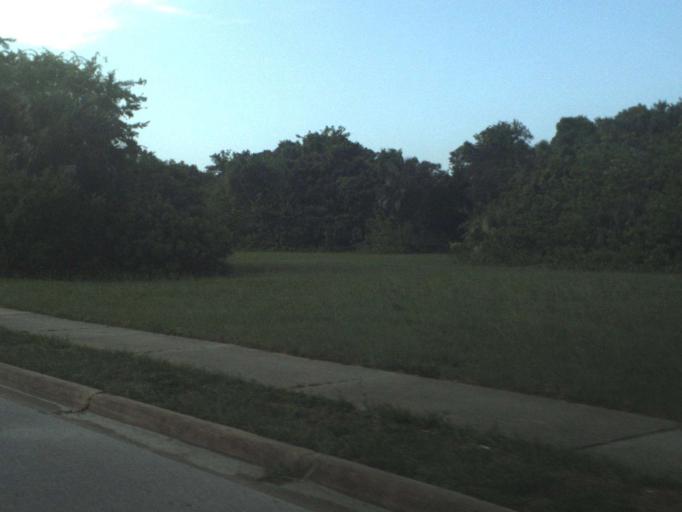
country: US
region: Florida
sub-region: Volusia County
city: South Daytona
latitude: 29.1629
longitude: -80.9971
